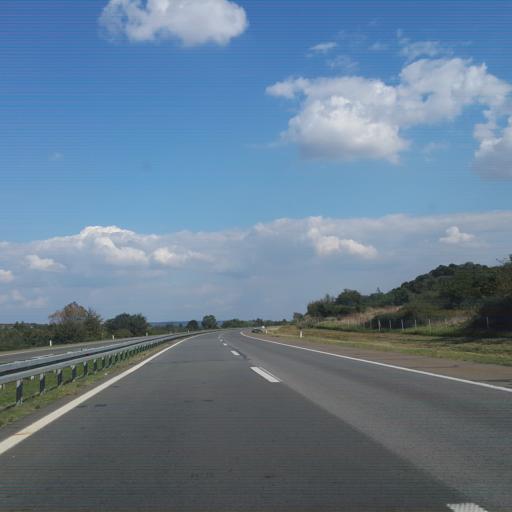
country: RS
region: Central Serbia
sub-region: Belgrade
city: Grocka
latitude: 44.5786
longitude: 20.7740
